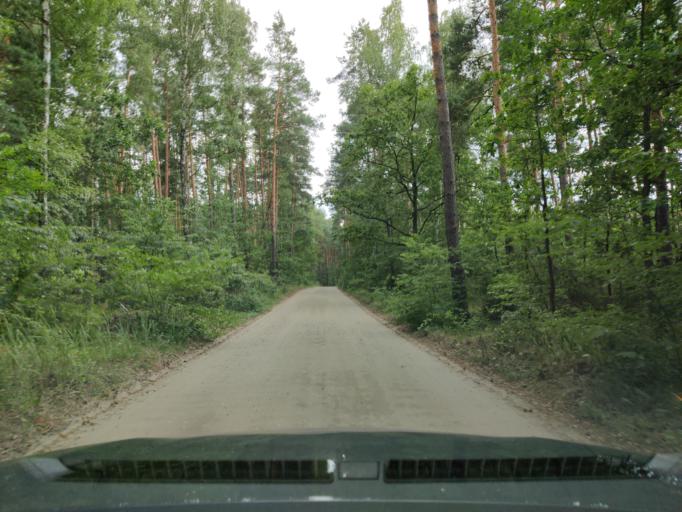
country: PL
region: Masovian Voivodeship
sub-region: Powiat pultuski
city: Pultusk
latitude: 52.7548
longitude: 21.1419
